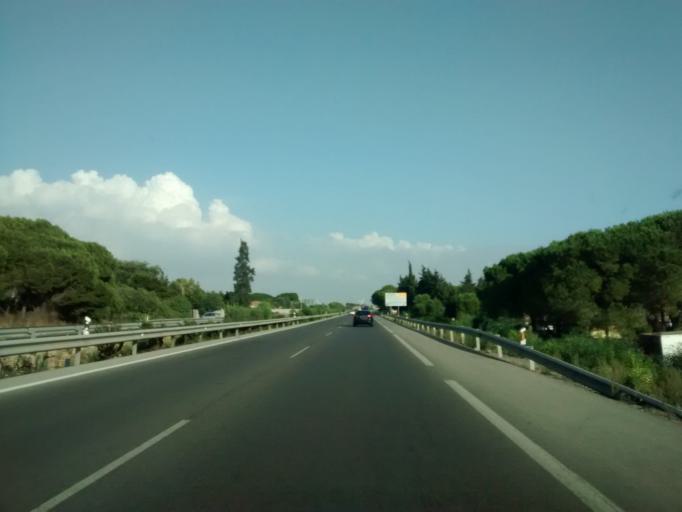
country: ES
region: Andalusia
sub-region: Provincia de Cadiz
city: Chiclana de la Frontera
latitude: 36.4430
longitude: -6.1347
